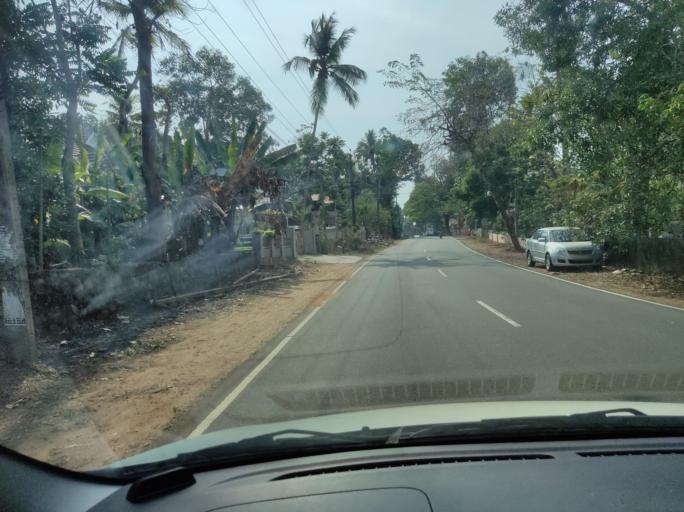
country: IN
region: Kerala
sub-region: Kottayam
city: Kottayam
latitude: 9.6750
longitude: 76.5194
